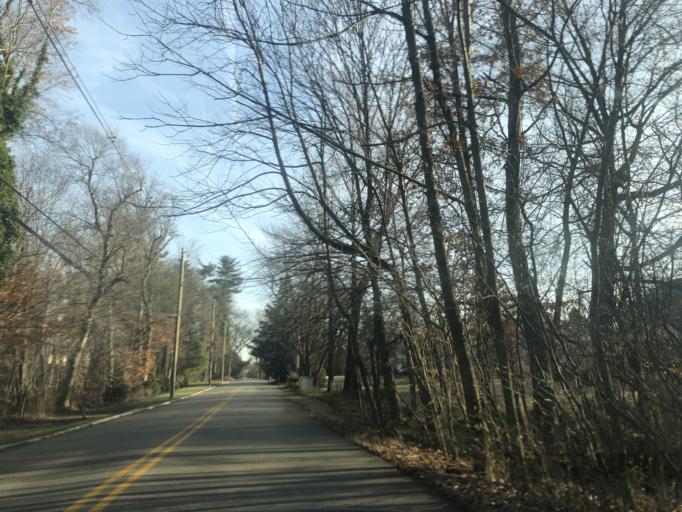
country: US
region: Pennsylvania
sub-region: Delaware County
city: Radnor
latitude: 40.0306
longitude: -75.3463
